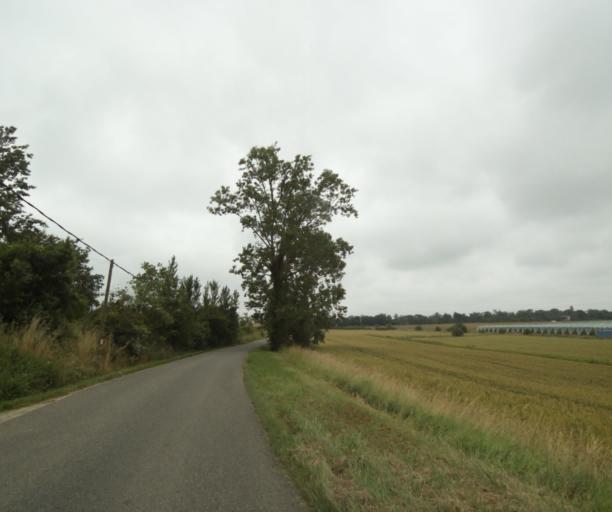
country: FR
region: Midi-Pyrenees
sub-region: Departement du Tarn-et-Garonne
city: Montbeton
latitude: 43.9936
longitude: 1.3056
